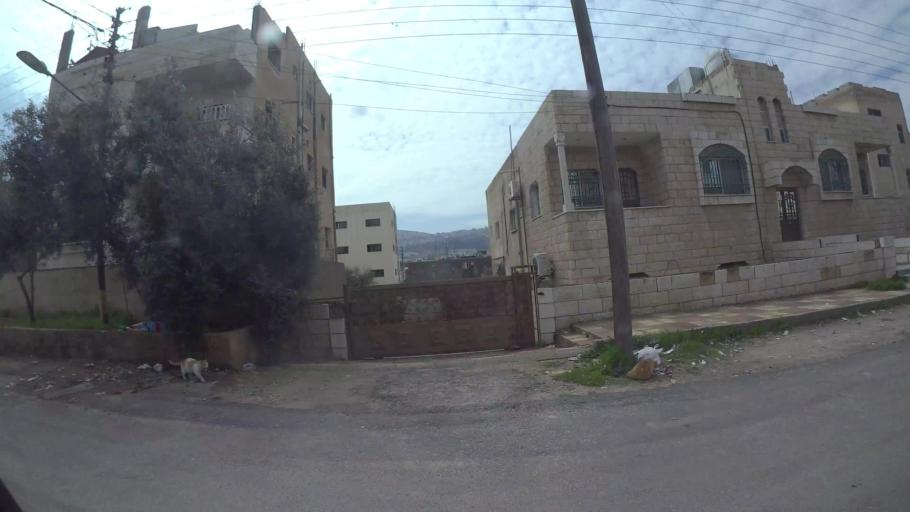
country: JO
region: Amman
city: Al Jubayhah
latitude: 32.0646
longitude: 35.8320
